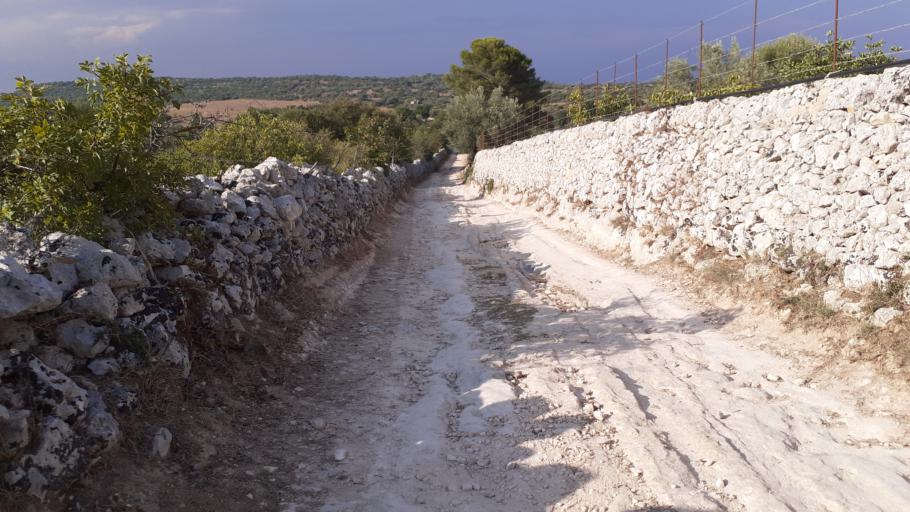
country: IT
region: Sicily
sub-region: Provincia di Siracusa
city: Canicattini Bagni
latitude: 36.9811
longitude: 15.0921
